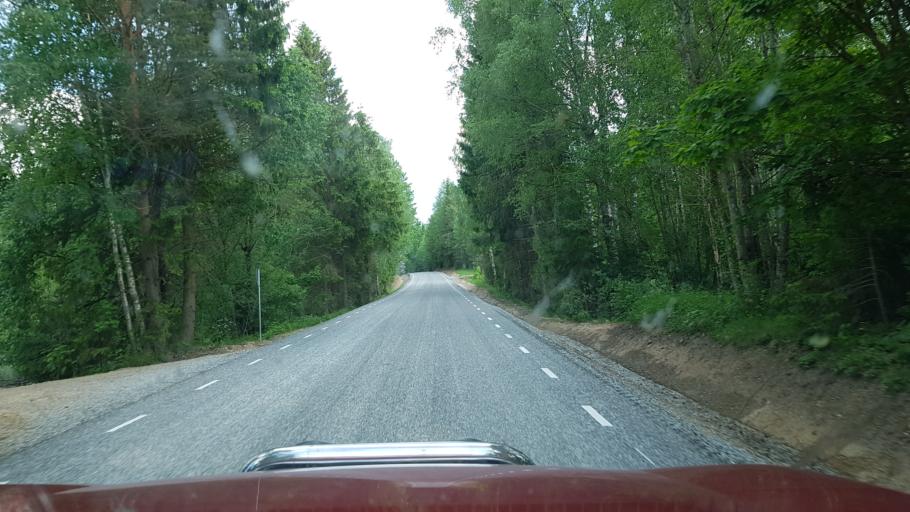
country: EE
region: Tartu
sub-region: UElenurme vald
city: Ulenurme
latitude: 58.1054
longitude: 26.7679
